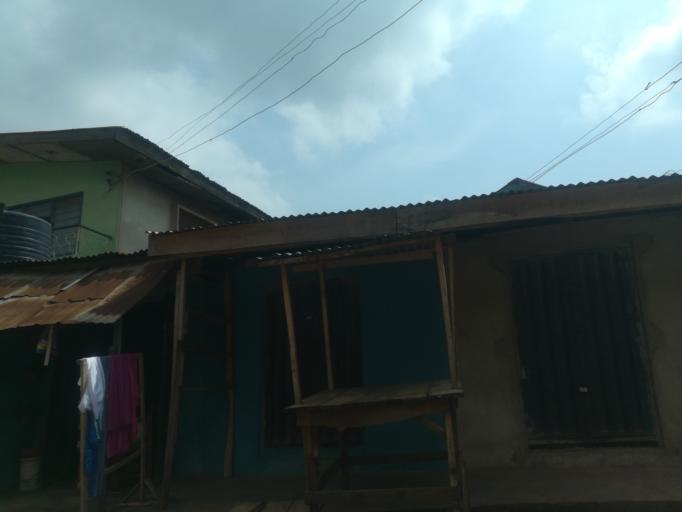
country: NG
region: Oyo
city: Ibadan
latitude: 7.4150
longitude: 3.9530
